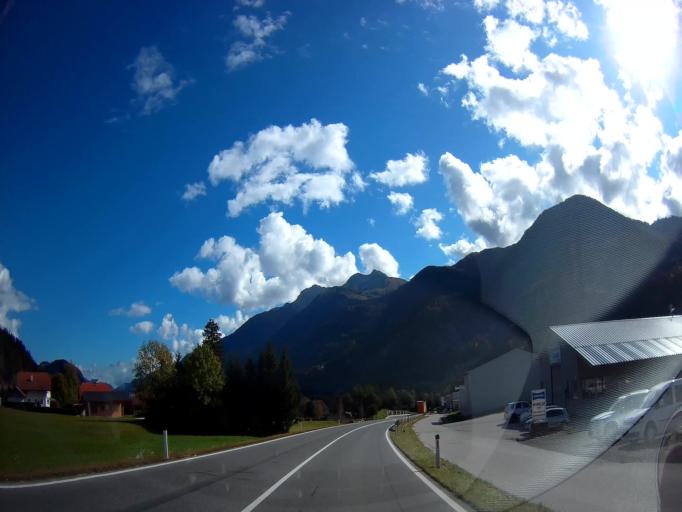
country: AT
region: Carinthia
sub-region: Politischer Bezirk Spittal an der Drau
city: Oberdrauburg
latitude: 46.7459
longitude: 12.9977
